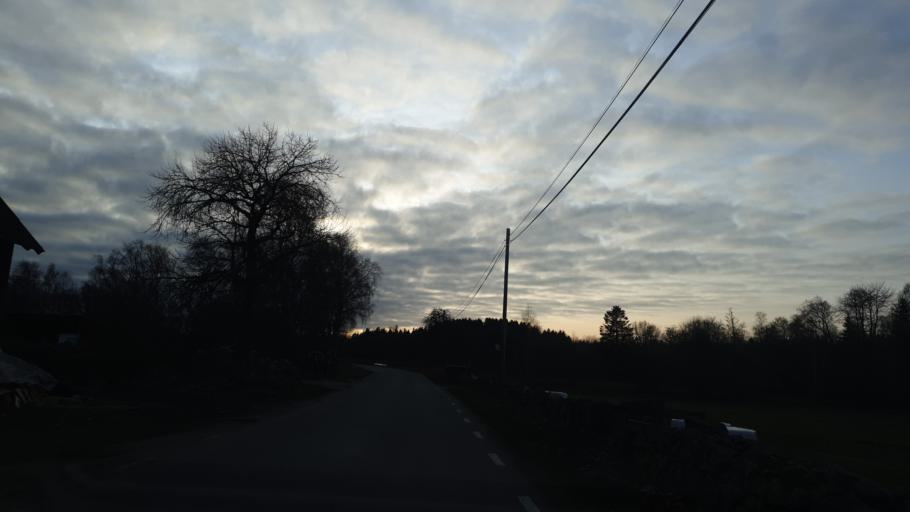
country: SE
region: Blekinge
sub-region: Karlskrona Kommun
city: Jaemjoe
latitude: 56.1832
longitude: 15.9395
